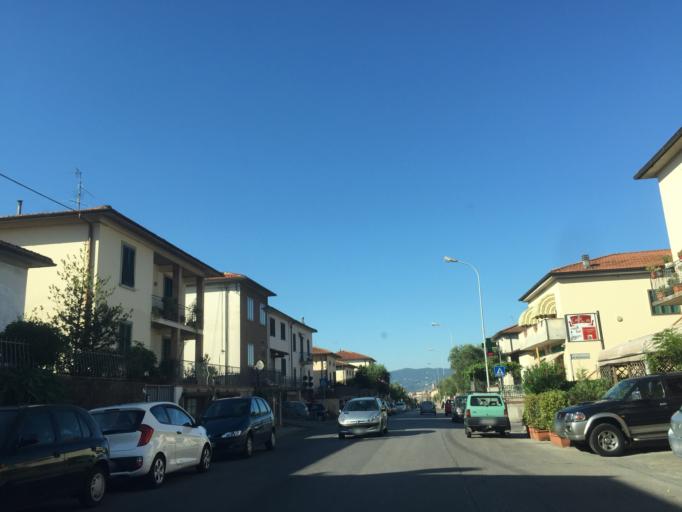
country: IT
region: Tuscany
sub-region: Provincia di Pistoia
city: Pistoia
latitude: 43.9508
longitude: 10.9384
